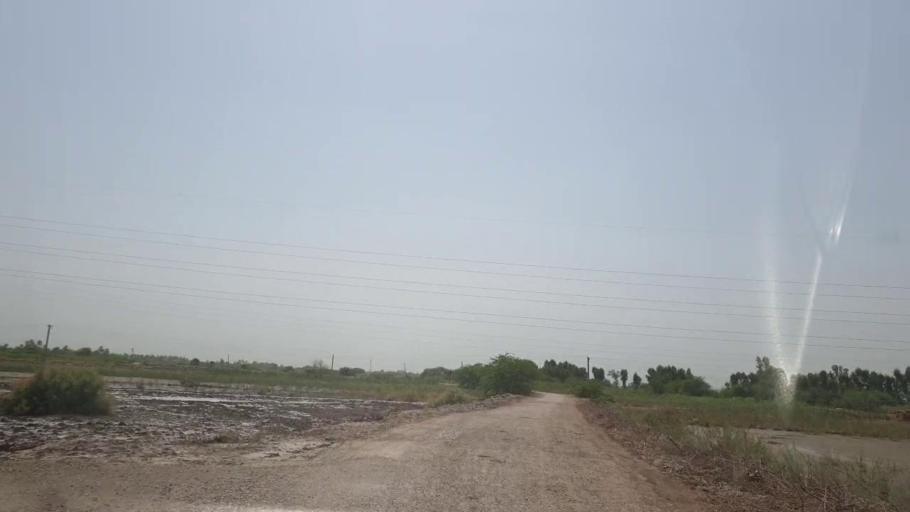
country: PK
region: Sindh
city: Gambat
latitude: 27.3160
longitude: 68.5370
